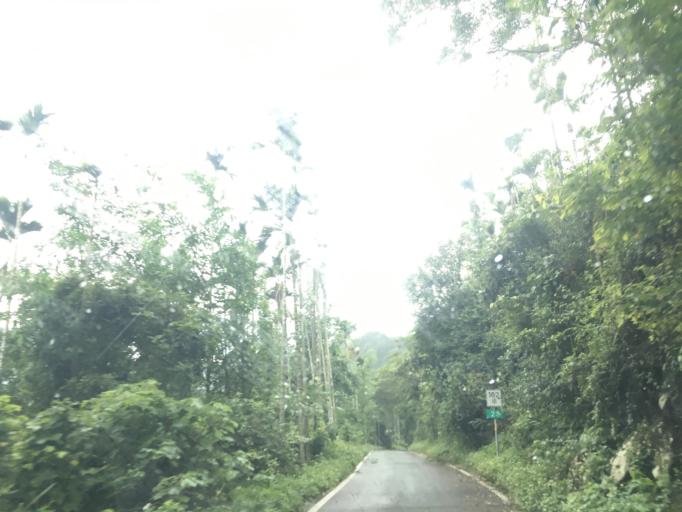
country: TW
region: Taiwan
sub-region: Yunlin
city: Douliu
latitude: 23.5702
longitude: 120.6400
